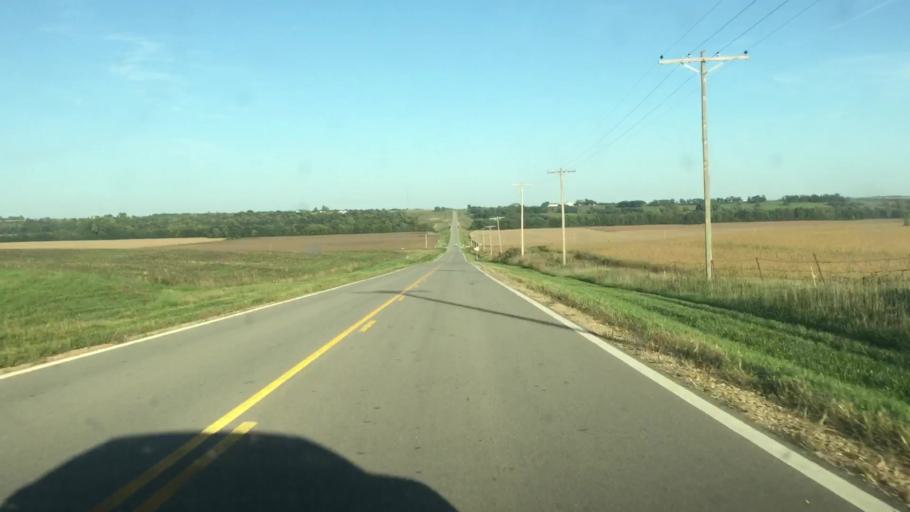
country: US
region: Kansas
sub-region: Brown County
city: Horton
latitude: 39.5875
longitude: -95.5711
